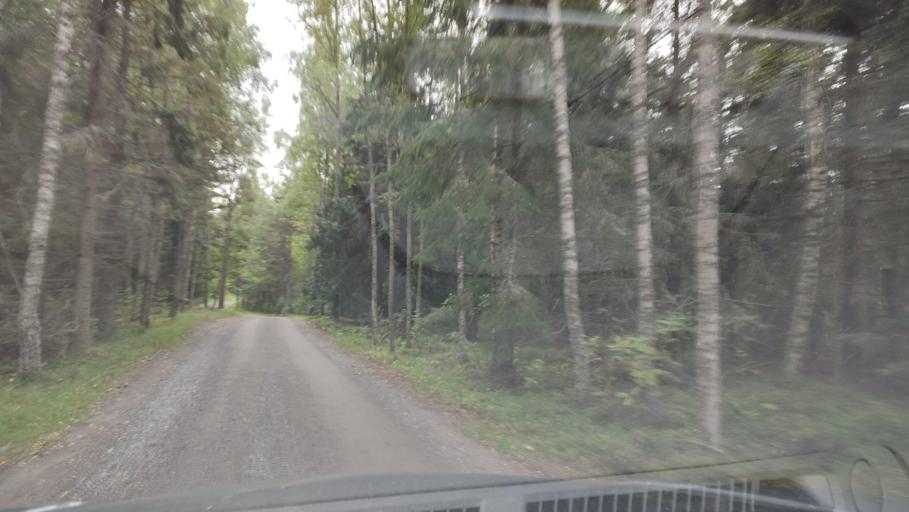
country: FI
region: Ostrobothnia
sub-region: Sydosterbotten
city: Kristinestad
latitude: 62.2492
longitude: 21.3243
